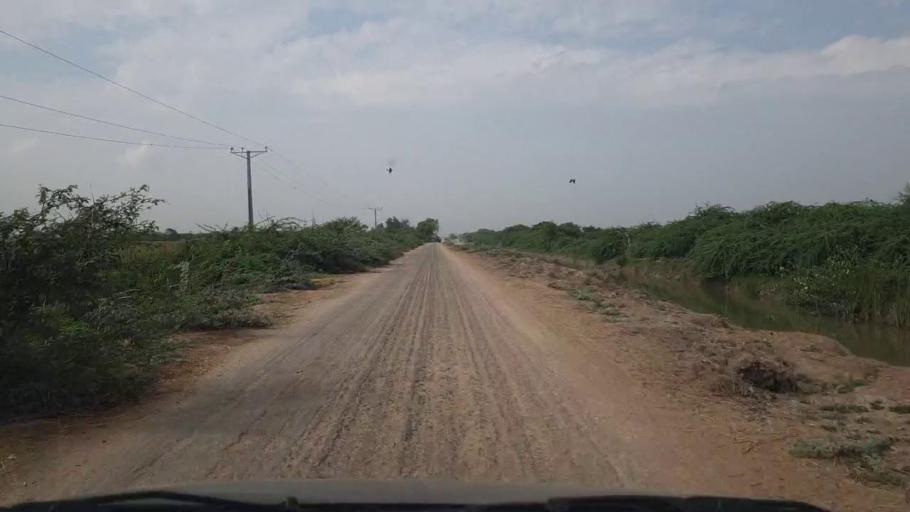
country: PK
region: Sindh
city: Kario
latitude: 24.6289
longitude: 68.5737
